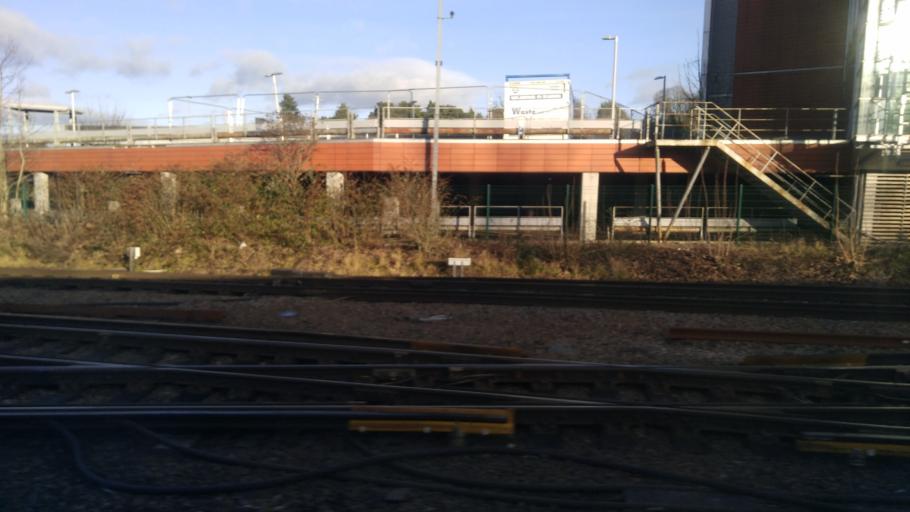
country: GB
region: England
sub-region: Kent
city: Sevenoaks
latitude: 51.2785
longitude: 0.1806
